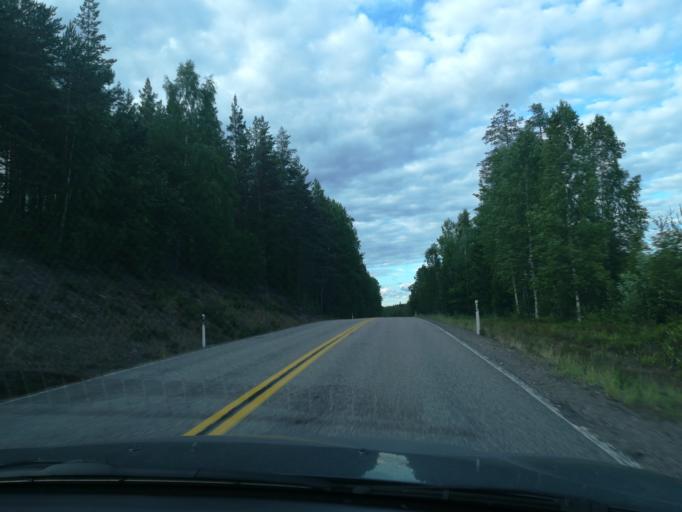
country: FI
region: Southern Savonia
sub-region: Mikkeli
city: Puumala
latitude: 61.5057
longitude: 27.8666
